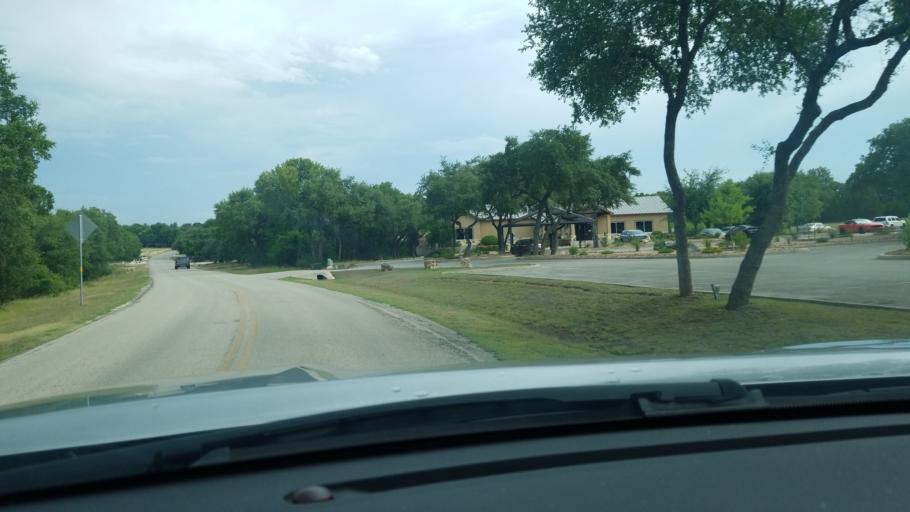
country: US
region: Texas
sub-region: Comal County
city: Bulverde
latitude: 29.8436
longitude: -98.4044
